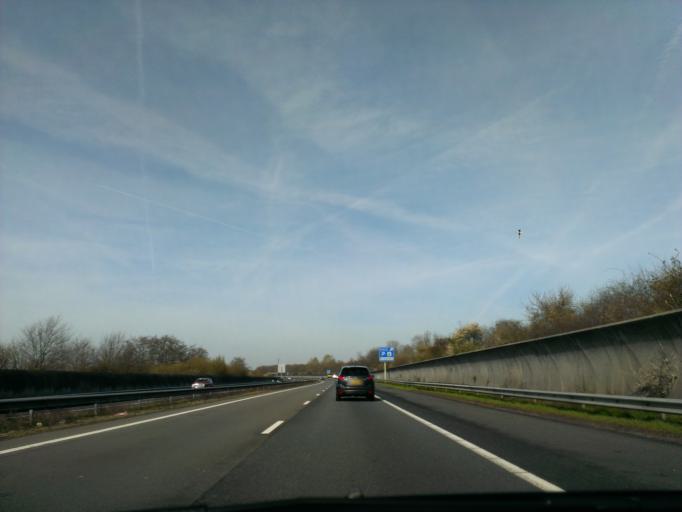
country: NL
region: Gelderland
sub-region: Gemeente Harderwijk
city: Harderwijk
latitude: 52.3315
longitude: 5.6060
